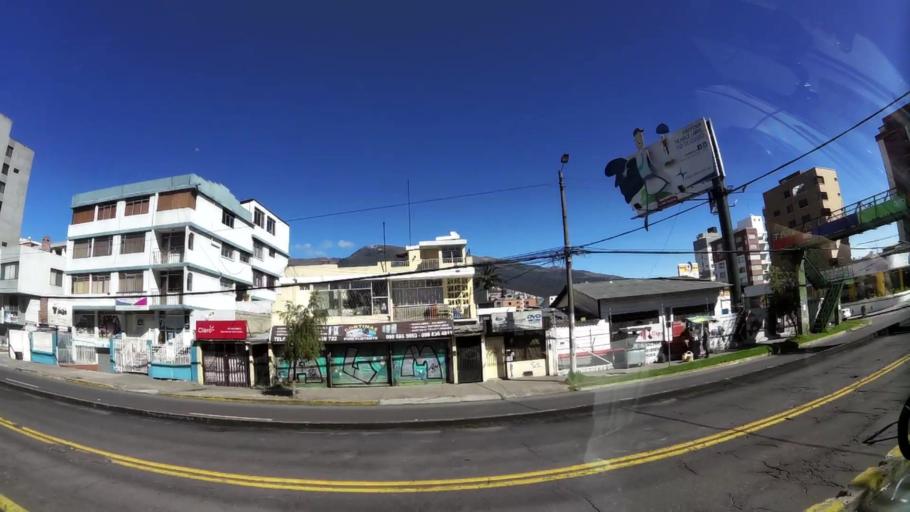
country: EC
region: Pichincha
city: Quito
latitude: -0.1750
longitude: -78.4773
